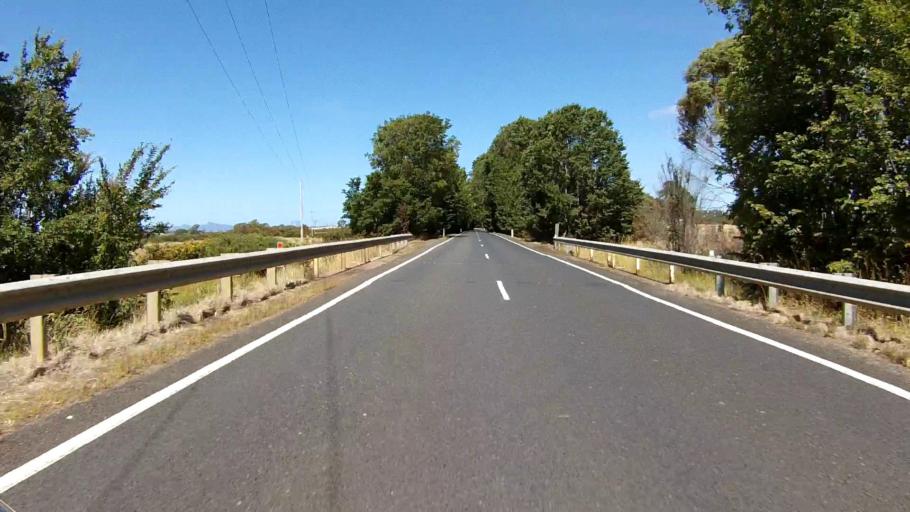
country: AU
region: Tasmania
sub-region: Break O'Day
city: St Helens
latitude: -42.0609
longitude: 148.0617
